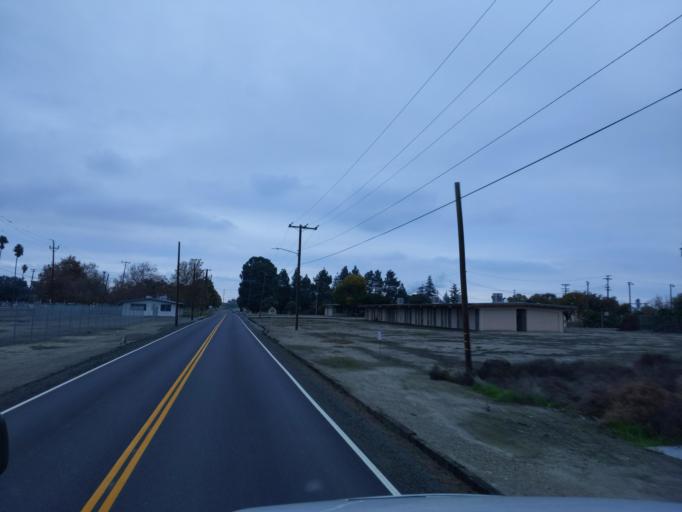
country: US
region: California
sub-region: San Joaquin County
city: Country Club
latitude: 37.9482
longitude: -121.3496
